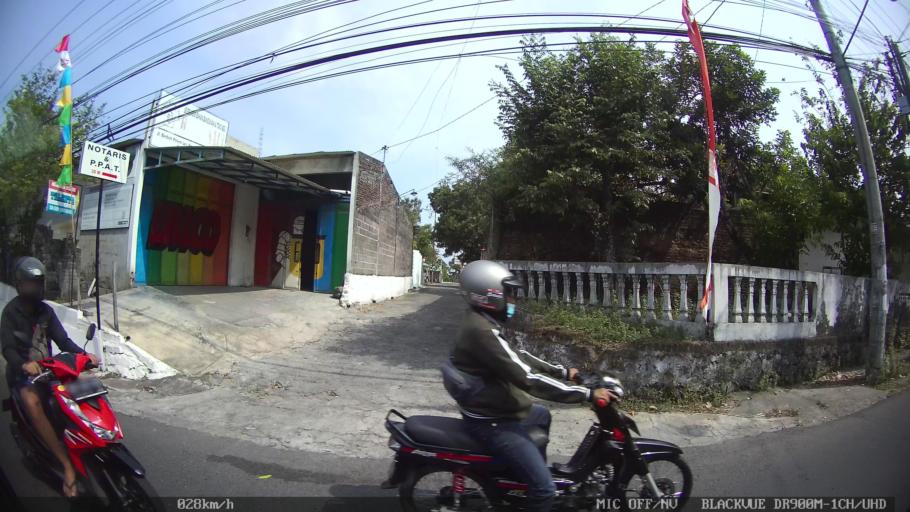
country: ID
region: Daerah Istimewa Yogyakarta
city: Depok
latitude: -7.8032
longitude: 110.4215
